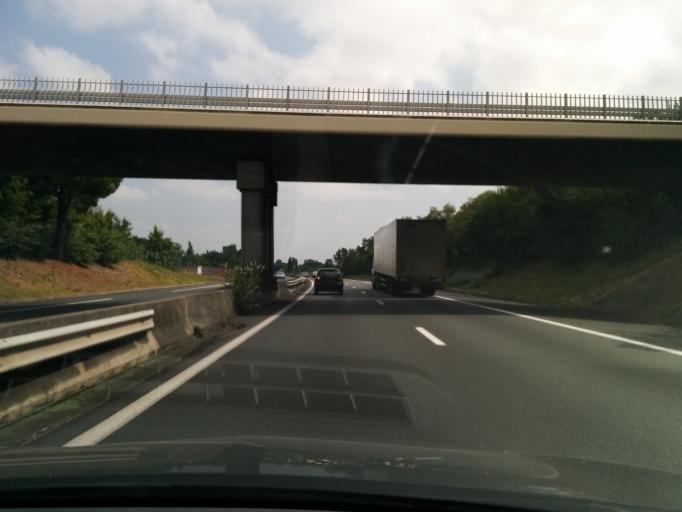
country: FR
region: Midi-Pyrenees
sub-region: Departement de la Haute-Garonne
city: Beaupuy
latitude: 43.6581
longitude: 1.5462
